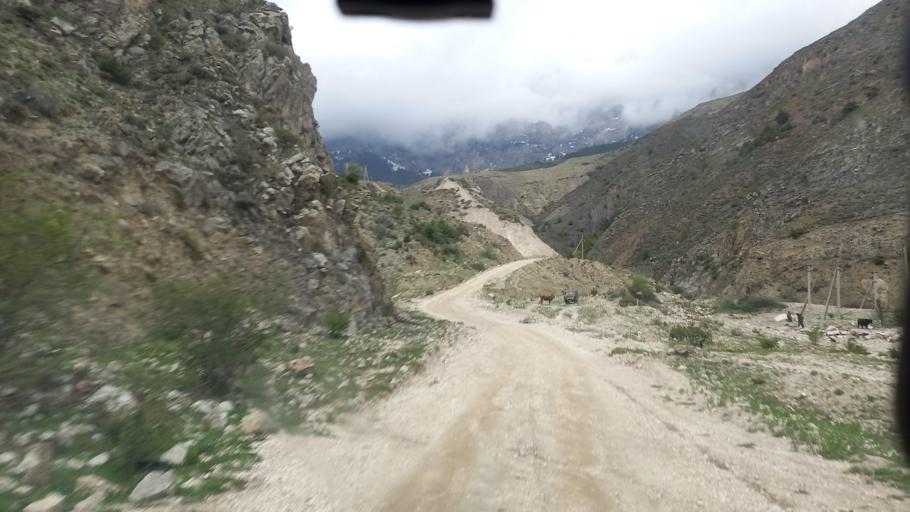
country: RU
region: North Ossetia
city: Mizur
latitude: 42.8548
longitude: 44.0745
